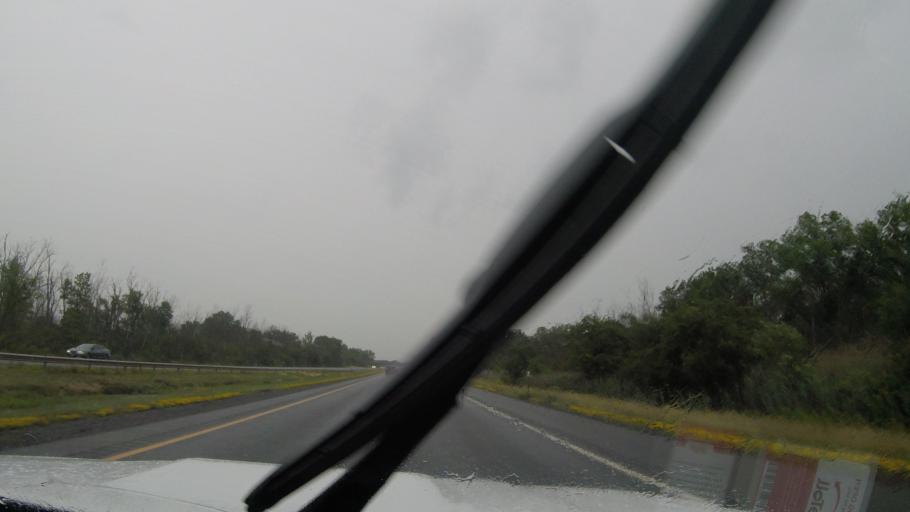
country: US
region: New York
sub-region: Cayuga County
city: Port Byron
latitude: 43.0138
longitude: -76.6900
